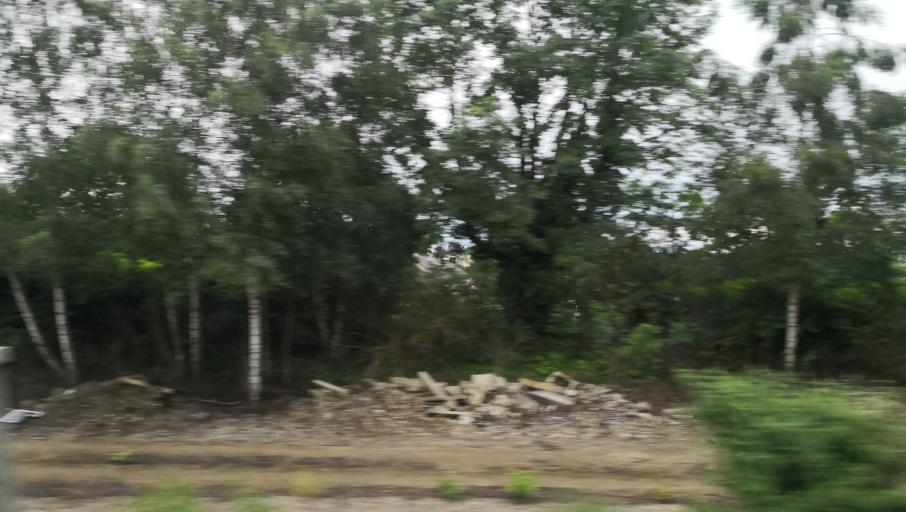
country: FR
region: Limousin
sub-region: Departement de la Haute-Vienne
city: Le Palais-sur-Vienne
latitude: 45.8498
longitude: 1.2958
